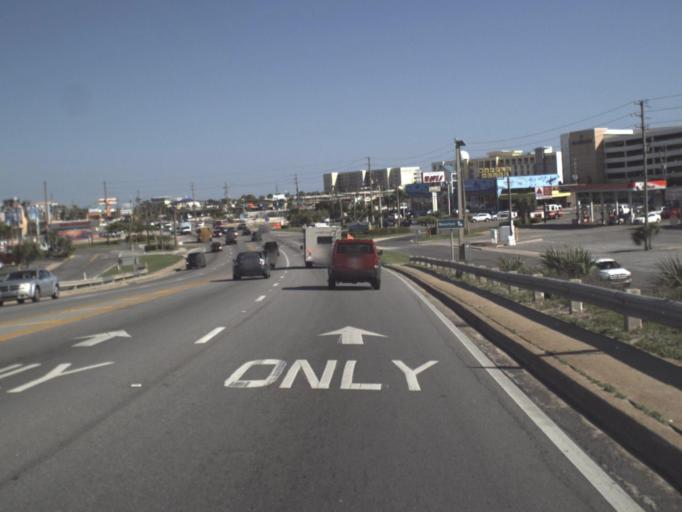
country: US
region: Florida
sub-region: Okaloosa County
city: Fort Walton Beach
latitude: 30.3992
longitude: -86.5992
